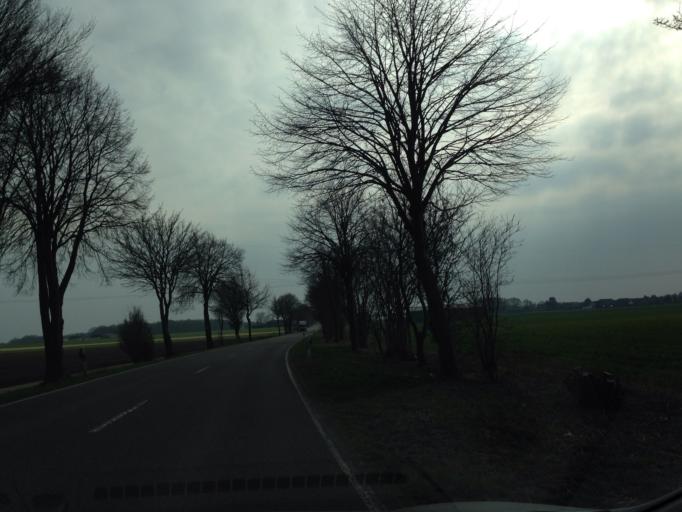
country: DE
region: North Rhine-Westphalia
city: Erkelenz
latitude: 51.0668
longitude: 6.2798
